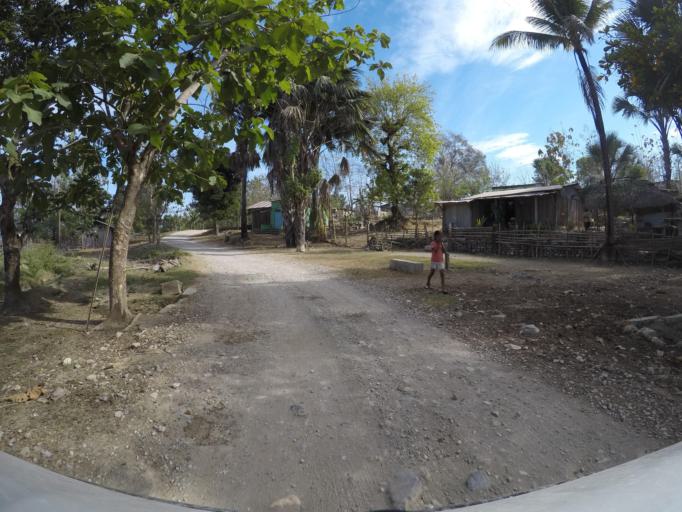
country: TL
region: Bobonaro
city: Maliana
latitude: -8.8842
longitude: 125.2089
